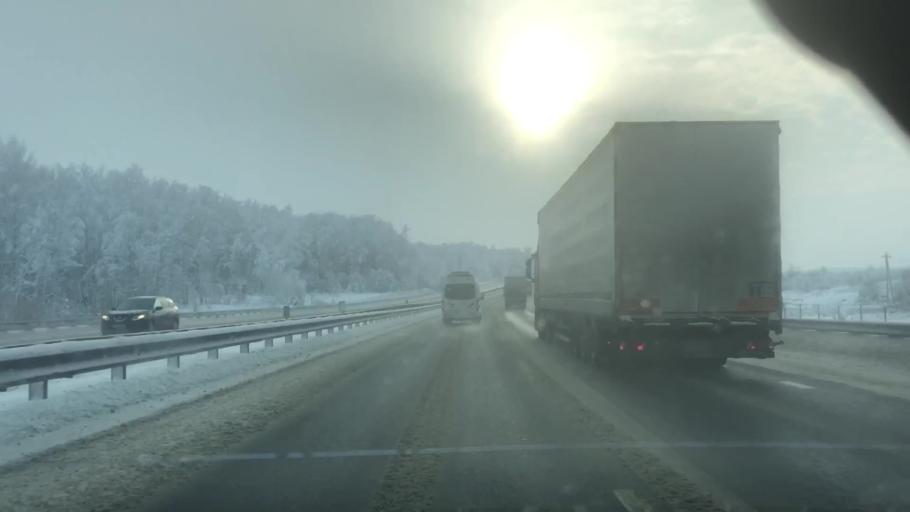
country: RU
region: Tula
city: Venev
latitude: 54.5165
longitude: 38.1705
